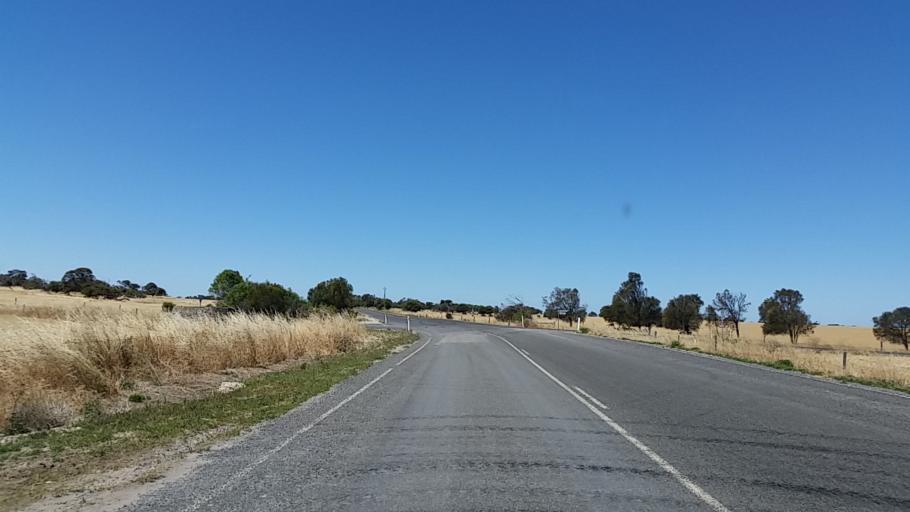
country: AU
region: South Australia
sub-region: Yorke Peninsula
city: Honiton
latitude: -35.0697
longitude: 137.5331
